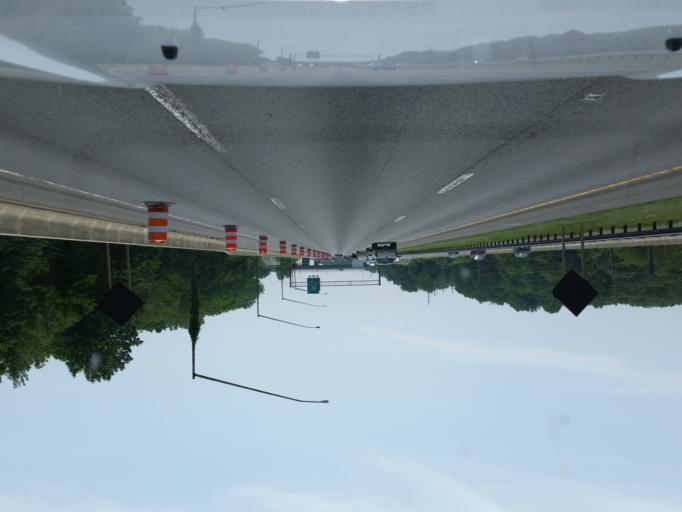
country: US
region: Maryland
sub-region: Montgomery County
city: Clarksburg
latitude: 39.2363
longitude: -77.2887
